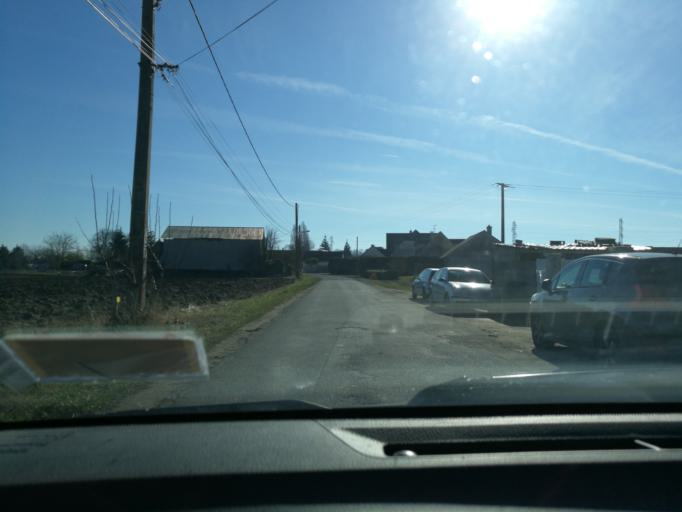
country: FR
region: Centre
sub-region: Departement du Loiret
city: Chaingy
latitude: 47.8817
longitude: 1.7848
